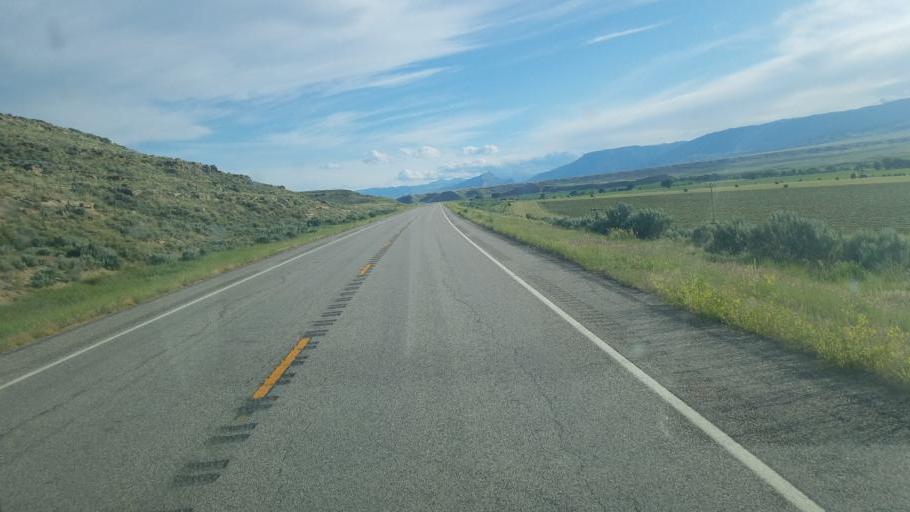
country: US
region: Montana
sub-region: Carbon County
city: Red Lodge
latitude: 45.0530
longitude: -109.0474
